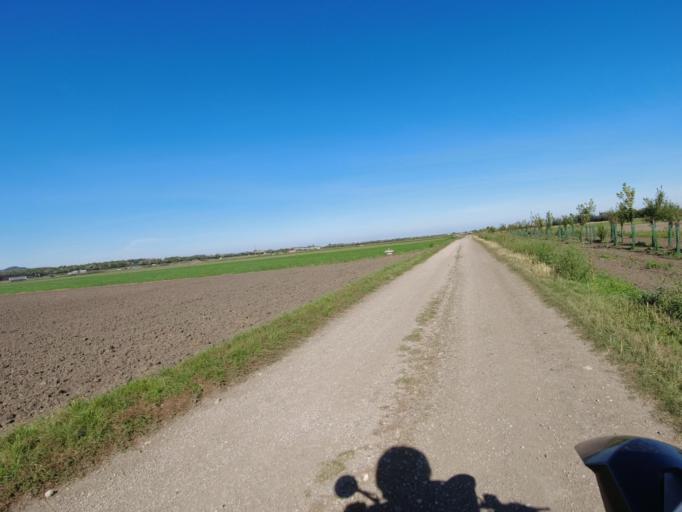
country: AT
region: Lower Austria
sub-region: Politischer Bezirk Baden
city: Trumau
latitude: 48.0186
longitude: 16.3338
